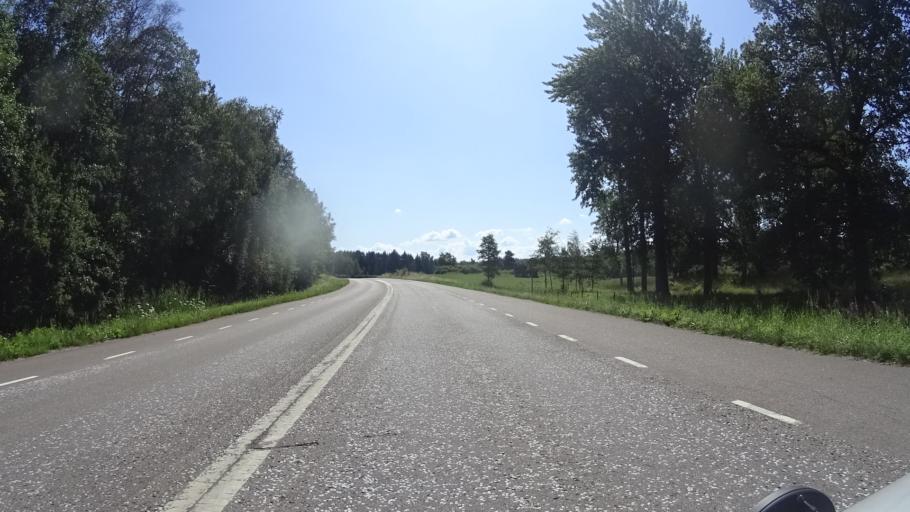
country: SE
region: OEstergoetland
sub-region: Vadstena Kommun
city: Herrestad
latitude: 58.3048
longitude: 14.9168
